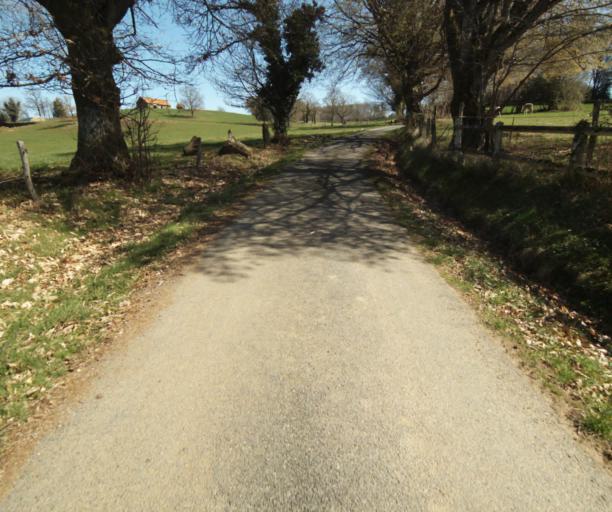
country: FR
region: Limousin
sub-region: Departement de la Correze
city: Uzerche
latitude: 45.3973
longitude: 1.6324
